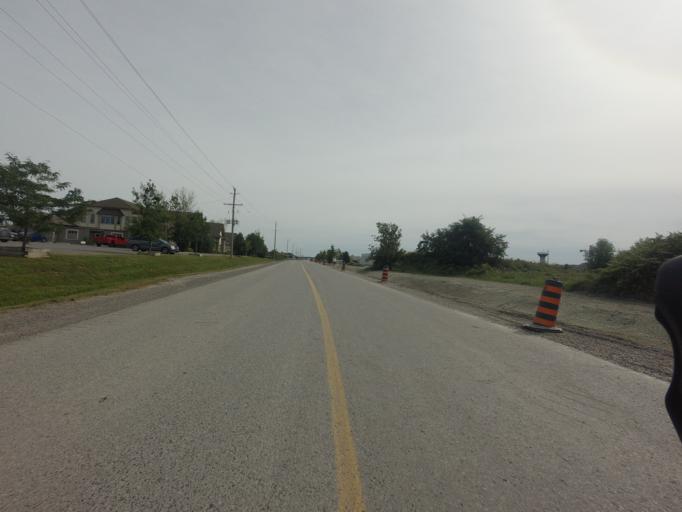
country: CA
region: Ontario
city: Carleton Place
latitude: 45.1433
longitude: -76.1289
